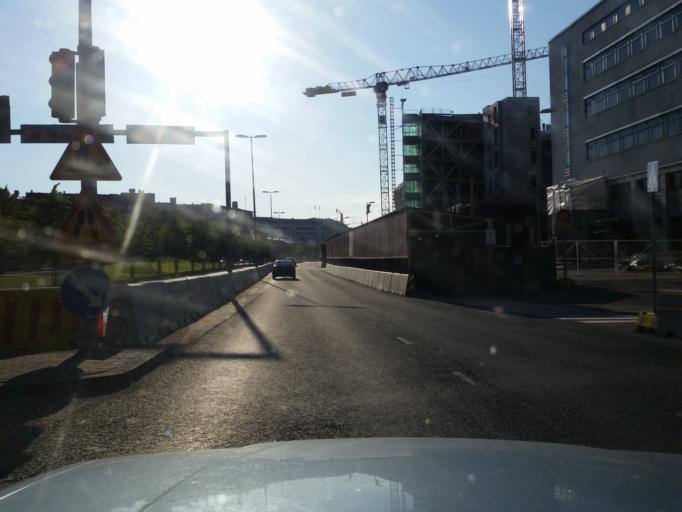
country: FI
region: Uusimaa
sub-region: Helsinki
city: Helsinki
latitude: 60.1899
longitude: 24.9611
